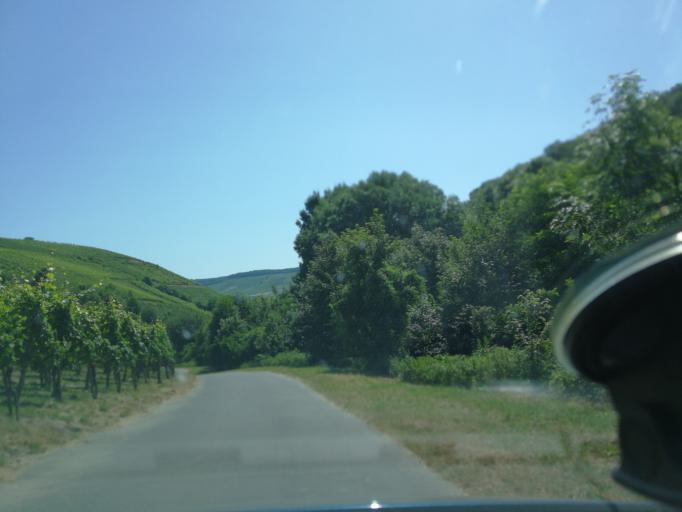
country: DE
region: Rheinland-Pfalz
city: Kesten
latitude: 49.8980
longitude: 6.9421
